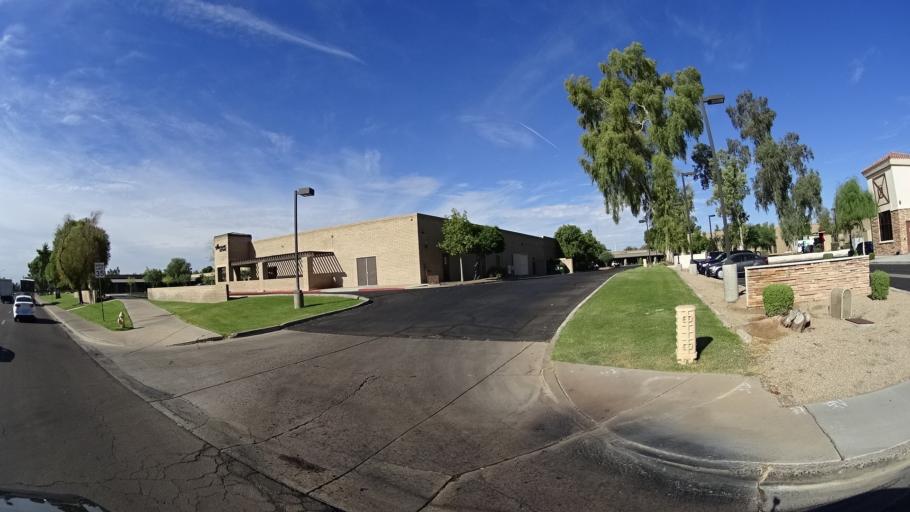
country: US
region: Arizona
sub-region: Maricopa County
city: Scottsdale
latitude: 33.4795
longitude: -111.9348
